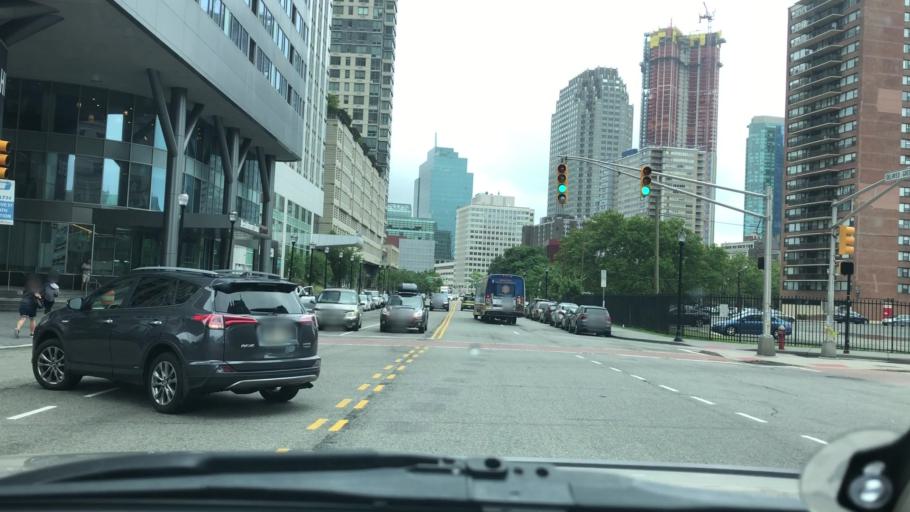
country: US
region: New Jersey
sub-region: Hudson County
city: Hoboken
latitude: 40.7190
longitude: -74.0415
